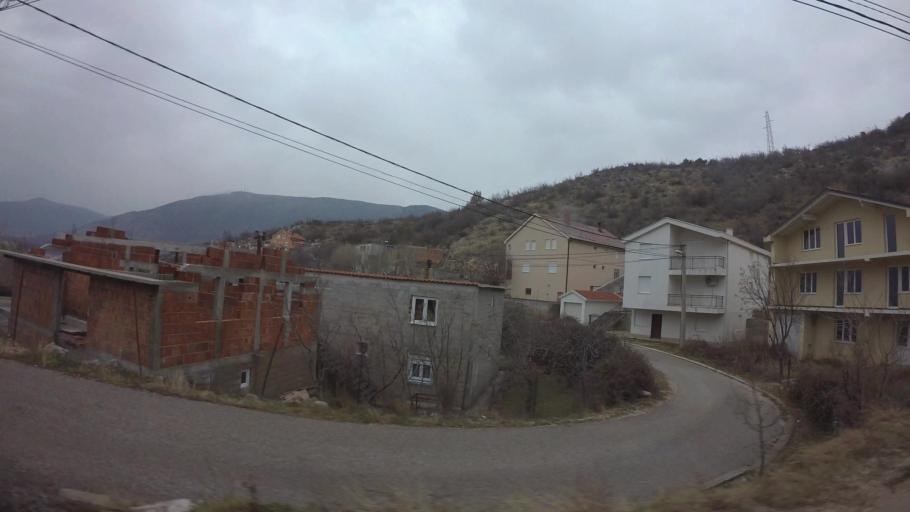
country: BA
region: Federation of Bosnia and Herzegovina
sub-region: Hercegovacko-Bosanski Kanton
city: Mostar
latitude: 43.3609
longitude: 17.8218
